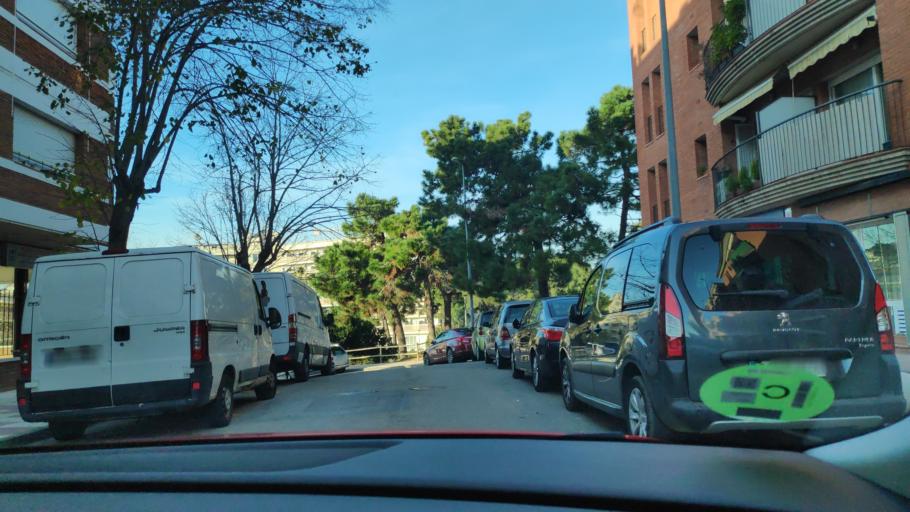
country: ES
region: Catalonia
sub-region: Provincia de Girona
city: Lloret de Mar
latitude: 41.7000
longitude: 2.8363
